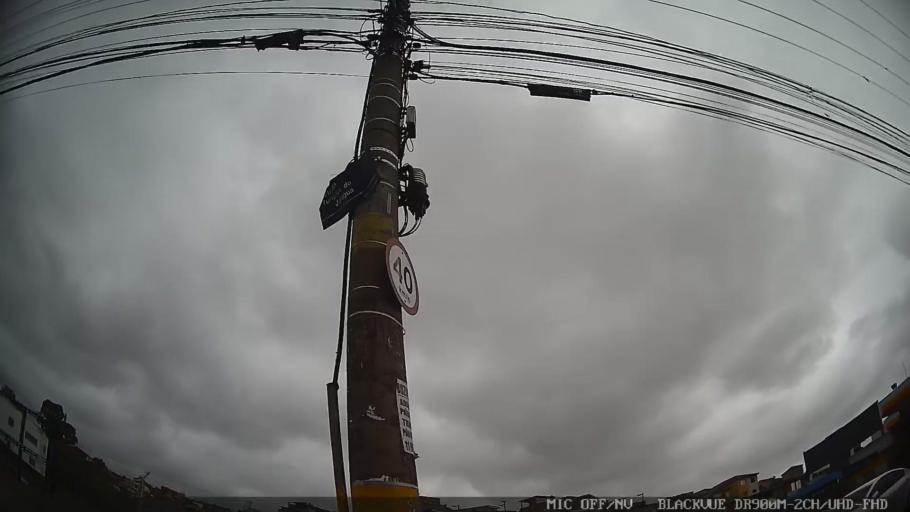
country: BR
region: Sao Paulo
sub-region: Osasco
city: Osasco
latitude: -23.4811
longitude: -46.7549
